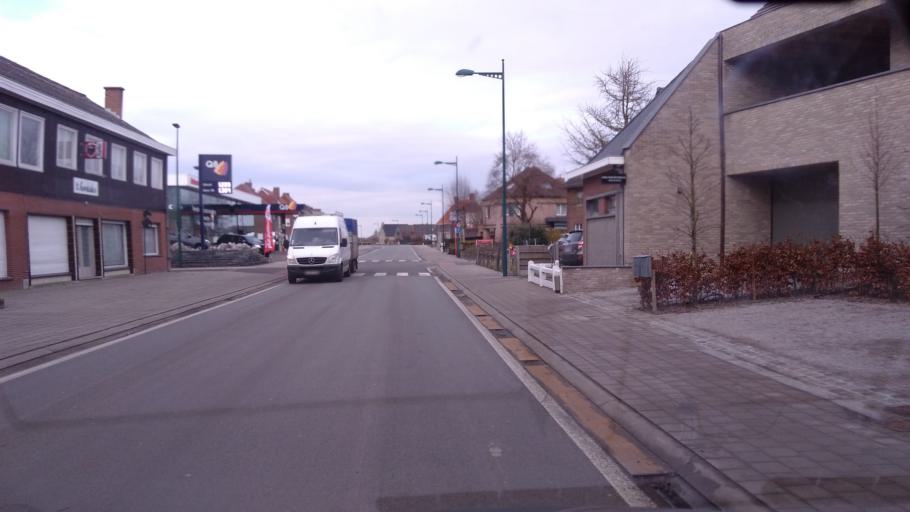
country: BE
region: Flanders
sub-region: Provincie Oost-Vlaanderen
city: Aalter
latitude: 51.0493
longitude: 3.4652
